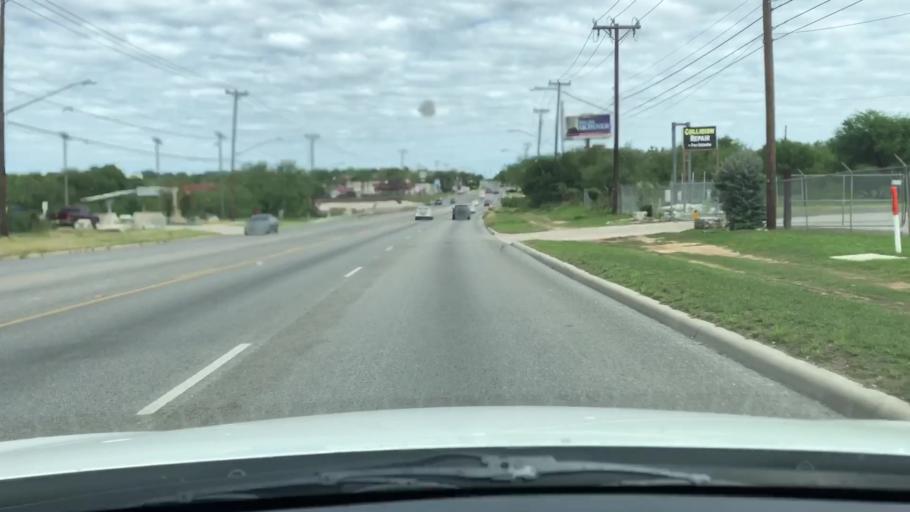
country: US
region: Texas
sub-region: Bexar County
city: Leon Valley
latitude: 29.4821
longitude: -98.6338
